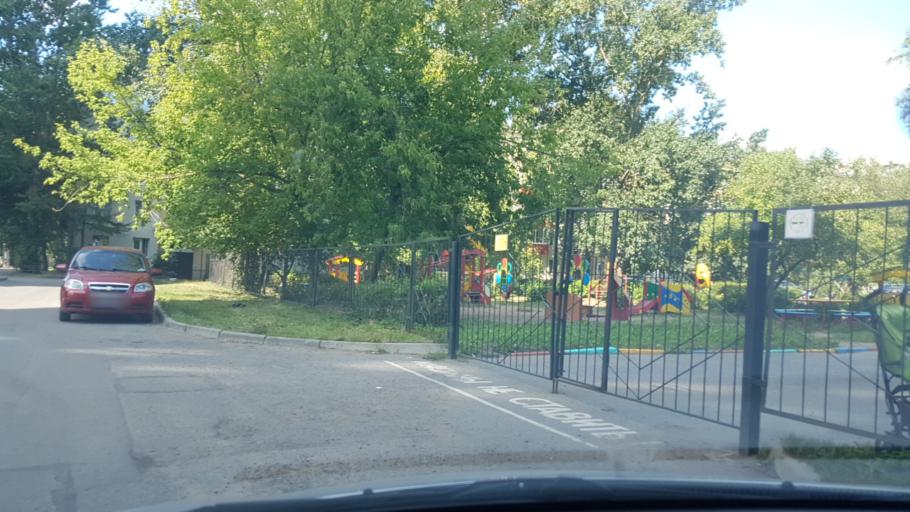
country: RU
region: St.-Petersburg
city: Sosnovaya Polyana
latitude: 59.8330
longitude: 30.1543
